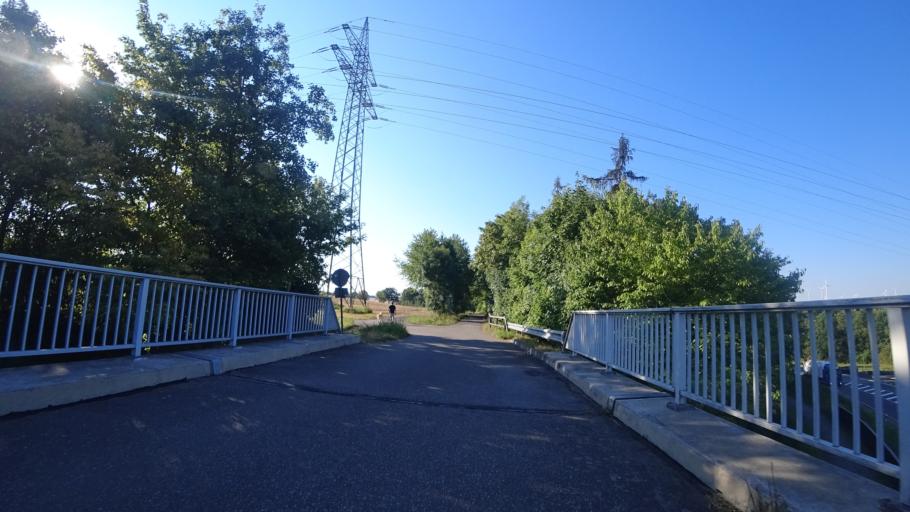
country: DE
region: Rheinland-Pfalz
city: Emmelshausen
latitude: 50.1454
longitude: 7.5623
